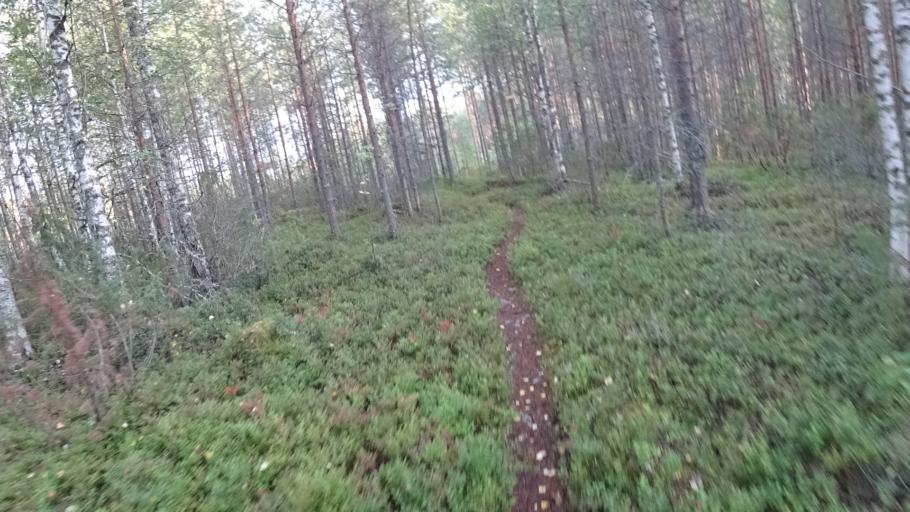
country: FI
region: North Karelia
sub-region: Joensuu
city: Ilomantsi
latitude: 62.6372
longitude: 31.0787
